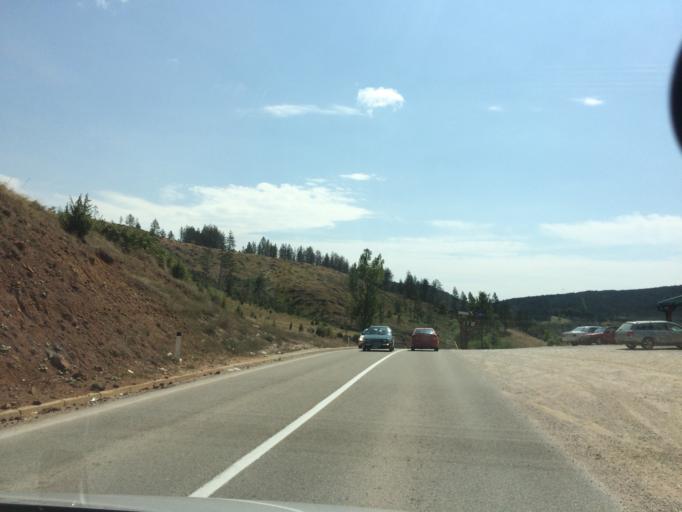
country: RS
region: Central Serbia
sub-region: Zlatiborski Okrug
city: Nova Varos
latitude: 43.5786
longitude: 19.7436
